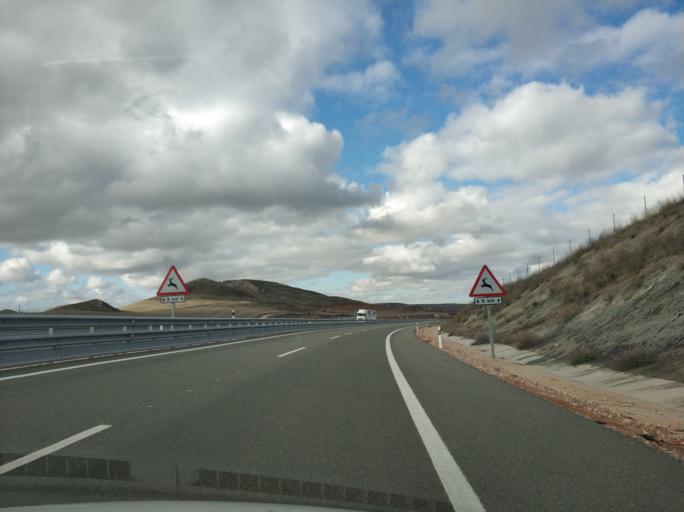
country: ES
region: Castille and Leon
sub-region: Provincia de Soria
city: Medinaceli
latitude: 41.1960
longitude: -2.4569
